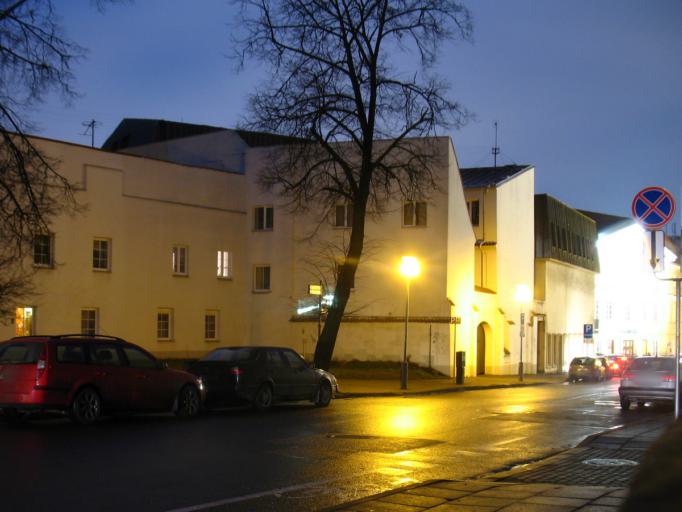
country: LT
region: Vilnius County
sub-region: Vilnius
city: Vilnius
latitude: 54.6758
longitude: 25.2863
